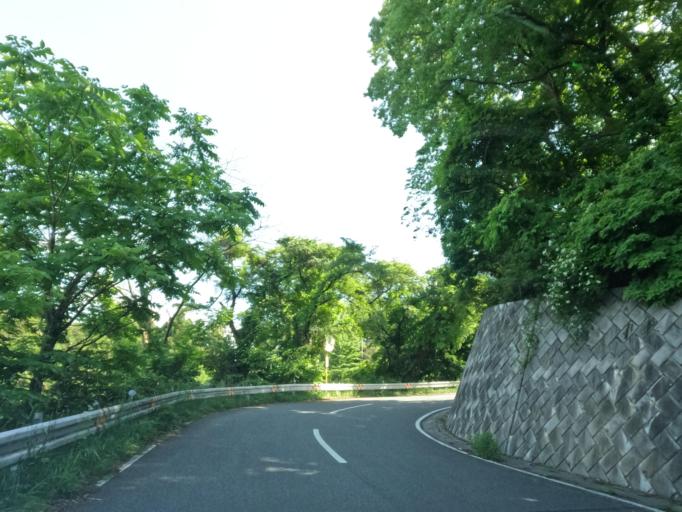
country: JP
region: Saitama
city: Yorii
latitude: 36.0477
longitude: 139.1588
